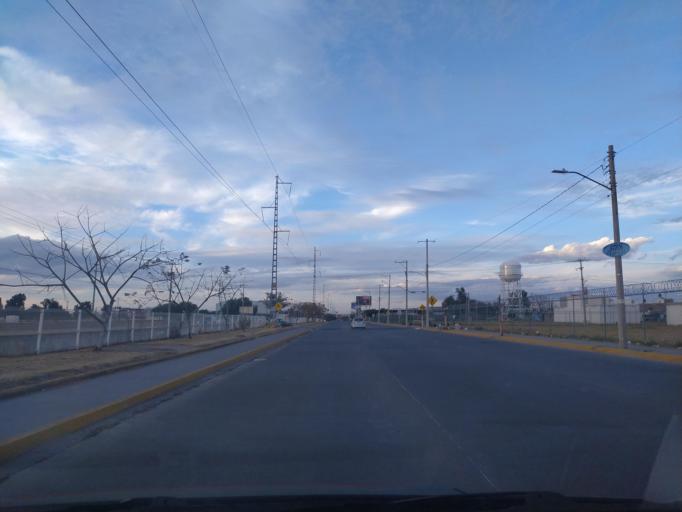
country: LA
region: Oudomxai
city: Muang La
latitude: 21.0182
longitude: 101.8696
